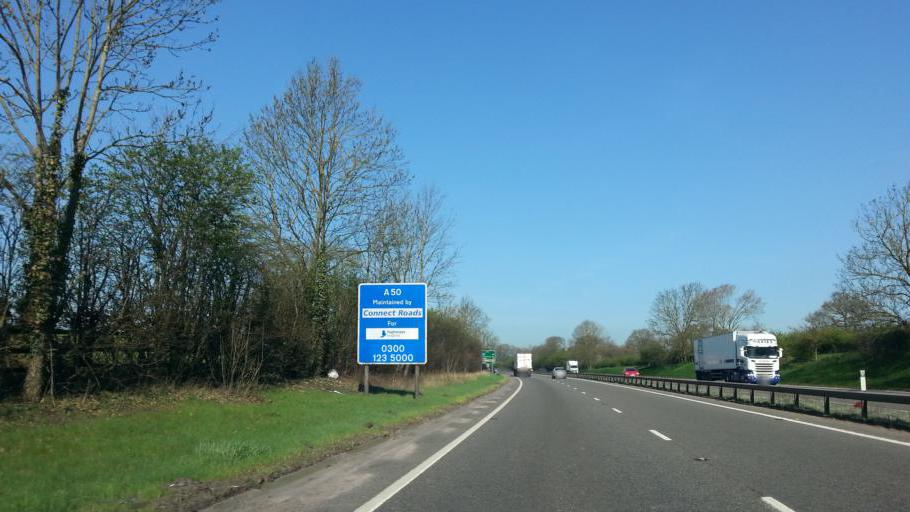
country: GB
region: England
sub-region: Derbyshire
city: Rodsley
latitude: 52.8876
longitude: -1.7606
